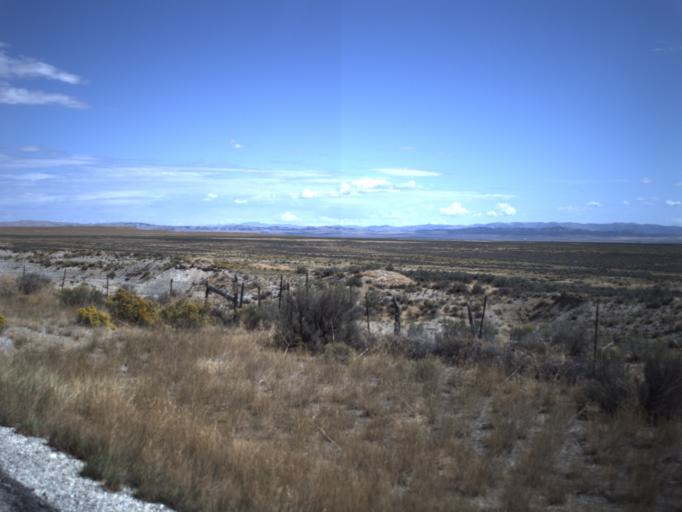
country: US
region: Idaho
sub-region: Oneida County
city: Malad City
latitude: 41.9390
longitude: -113.0850
